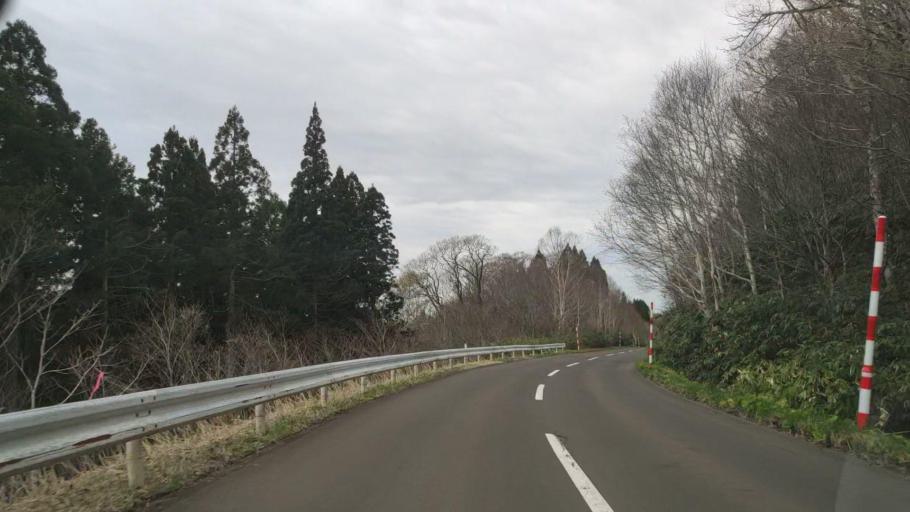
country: JP
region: Akita
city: Hanawa
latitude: 40.4091
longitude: 140.8168
